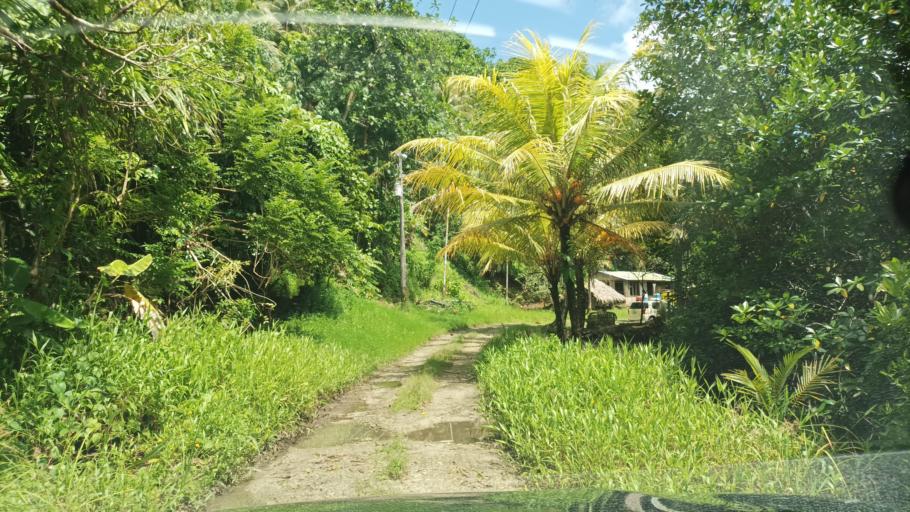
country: FM
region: Pohnpei
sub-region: Sokehs Municipality
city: Palikir - National Government Center
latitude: 6.9478
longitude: 158.1589
